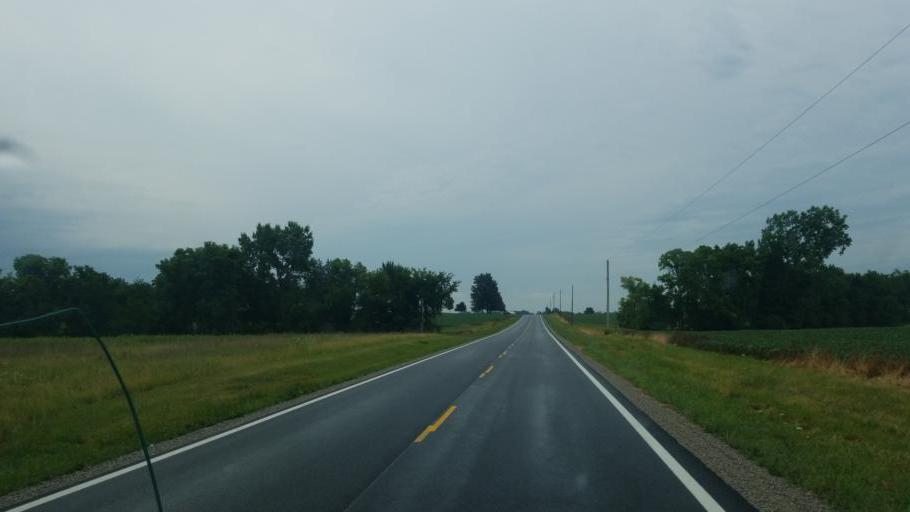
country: US
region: Ohio
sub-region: Williams County
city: Edgerton
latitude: 41.3797
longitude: -84.6697
